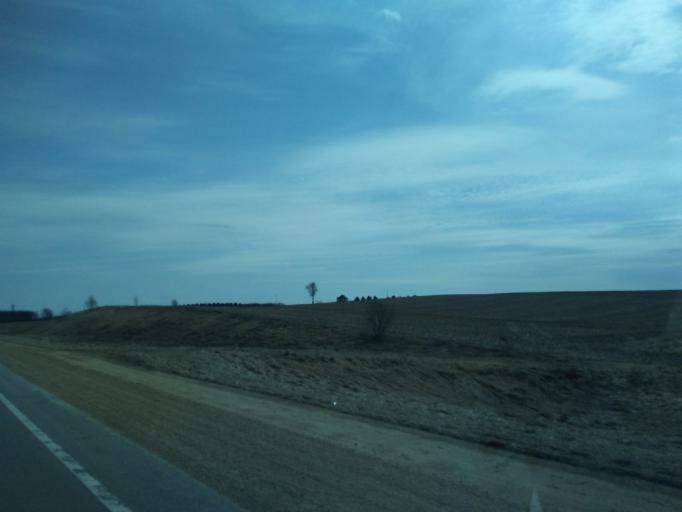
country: US
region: Iowa
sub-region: Winneshiek County
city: Decorah
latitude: 43.3763
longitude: -91.8156
